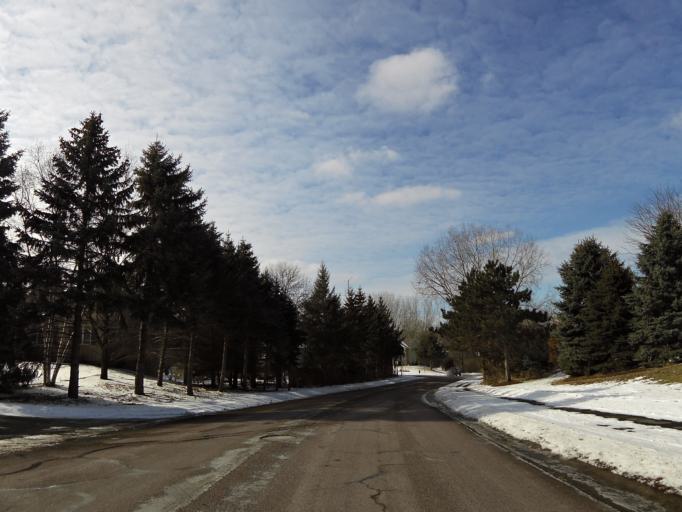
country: US
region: Minnesota
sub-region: Hennepin County
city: Eden Prairie
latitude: 44.8172
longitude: -93.4267
